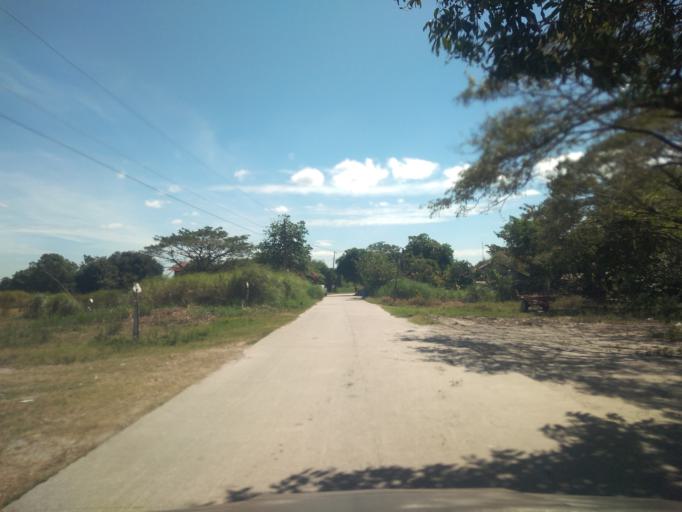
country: PH
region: Central Luzon
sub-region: Province of Pampanga
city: San Basilio
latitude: 15.0334
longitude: 120.6058
